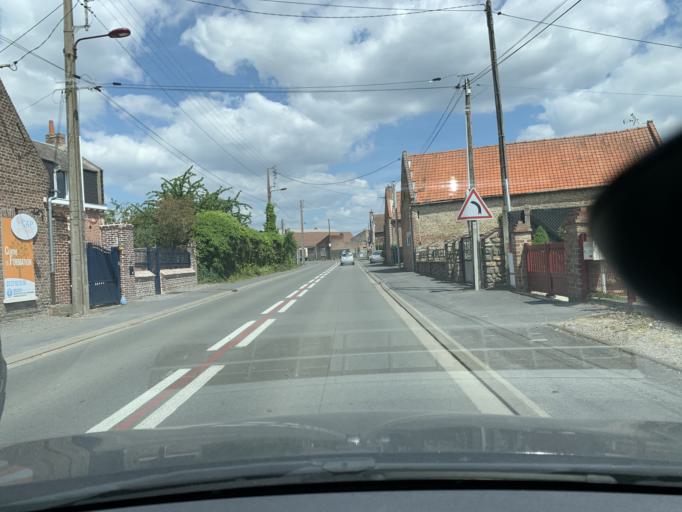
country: FR
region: Nord-Pas-de-Calais
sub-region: Departement du Nord
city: Goeulzin
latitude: 50.3170
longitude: 3.0972
